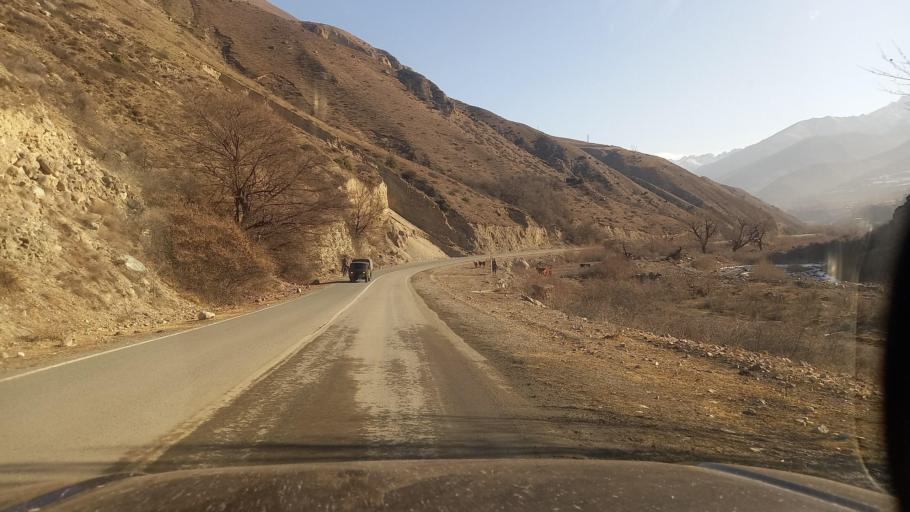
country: RU
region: Ingushetiya
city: Dzhayrakh
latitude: 42.8428
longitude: 44.6536
